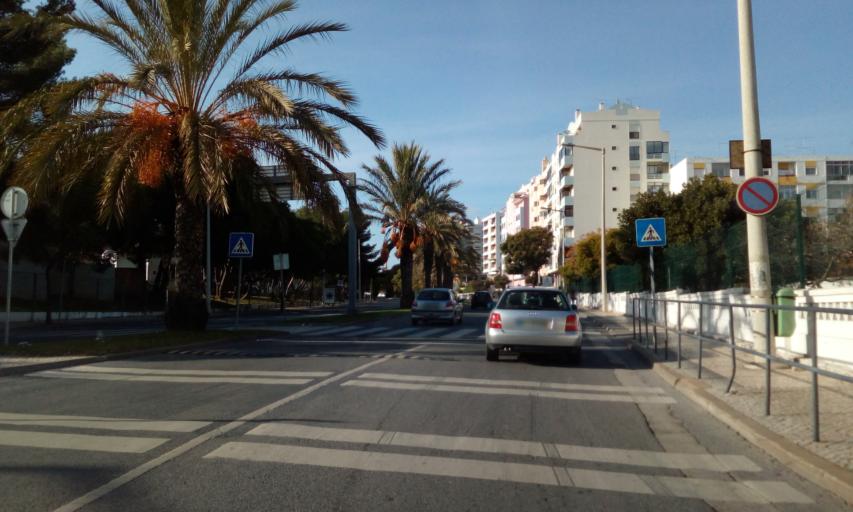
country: PT
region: Faro
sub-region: Faro
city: Faro
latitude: 37.0244
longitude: -7.9266
